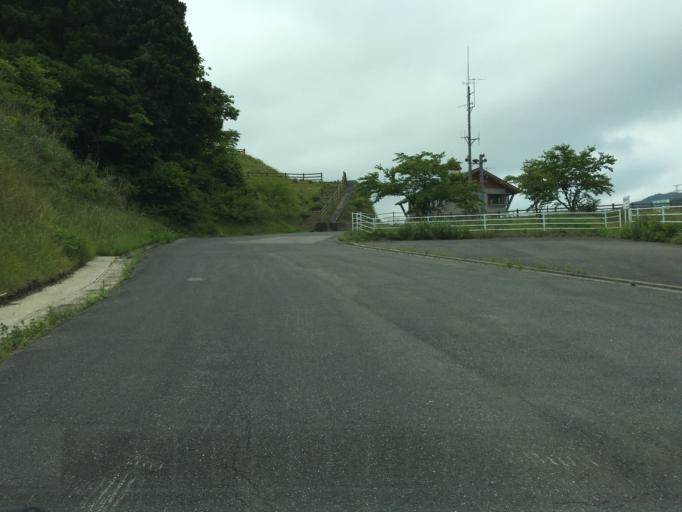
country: JP
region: Miyagi
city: Marumori
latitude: 37.7960
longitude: 140.7719
